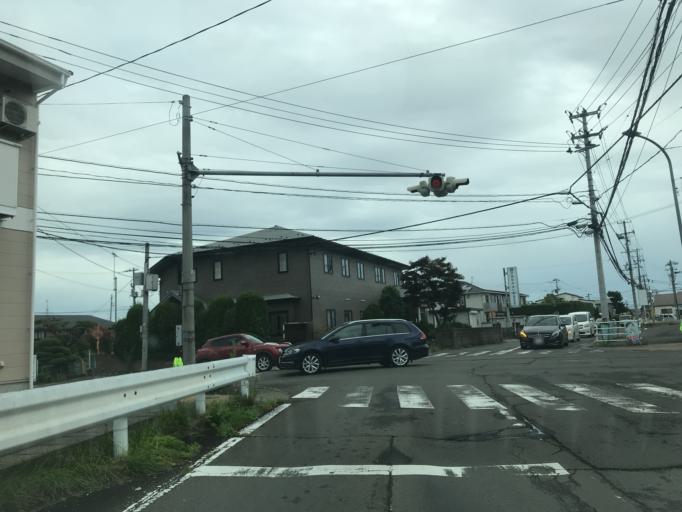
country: JP
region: Miyagi
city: Sendai-shi
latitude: 38.3169
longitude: 140.8701
